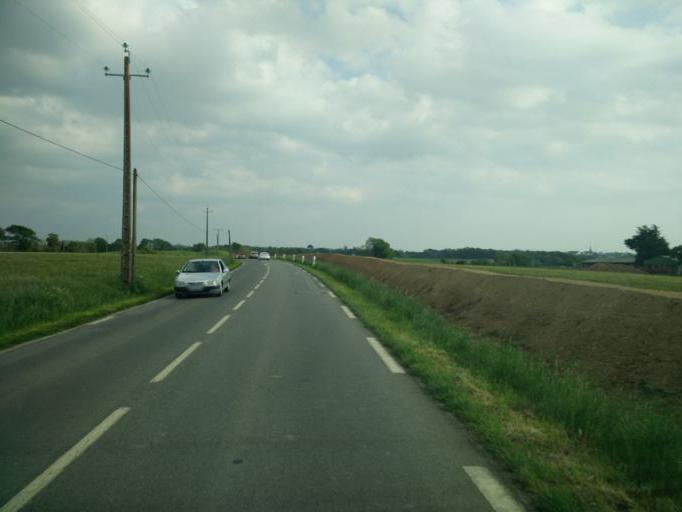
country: FR
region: Brittany
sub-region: Departement du Morbihan
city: Ploemeur
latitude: 47.7541
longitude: -3.4203
